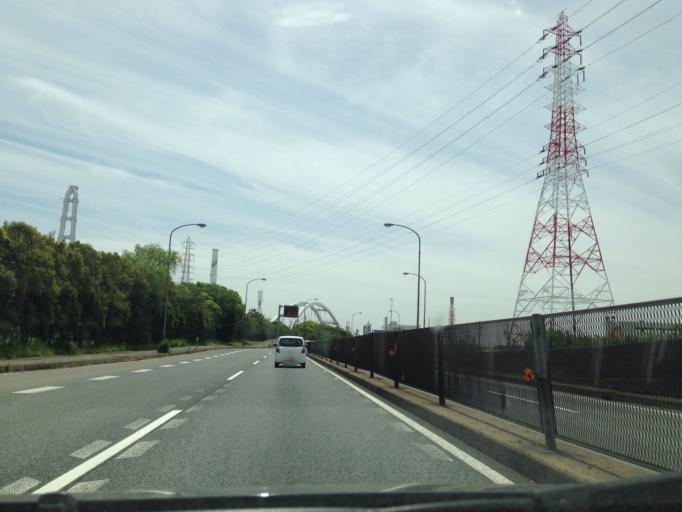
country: JP
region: Mie
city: Yokkaichi
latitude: 34.9811
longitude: 136.6444
